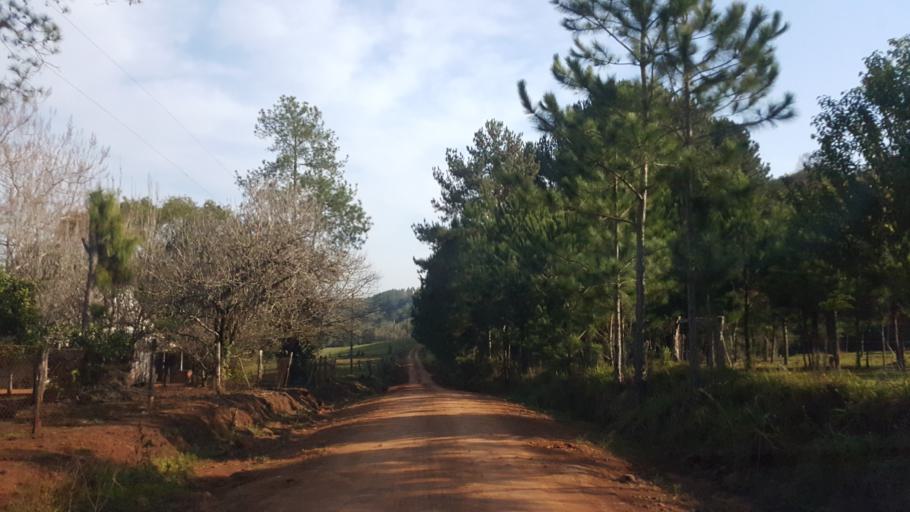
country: AR
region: Misiones
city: Capiovi
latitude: -26.9147
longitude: -55.0819
